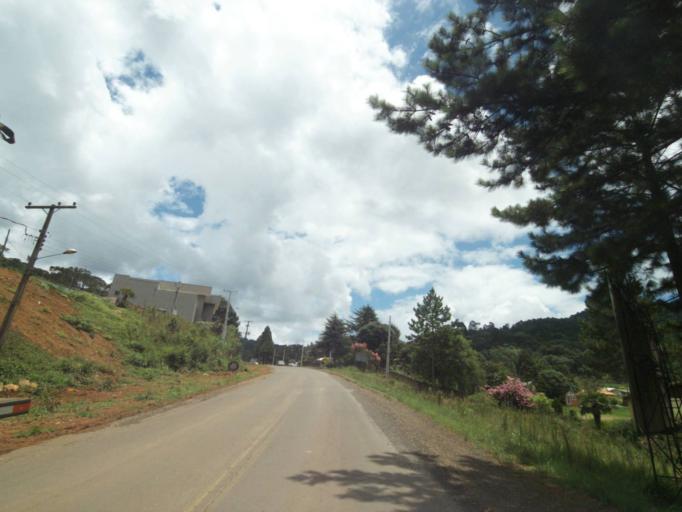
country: BR
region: Parana
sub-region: Pinhao
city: Pinhao
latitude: -26.1565
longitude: -51.5658
